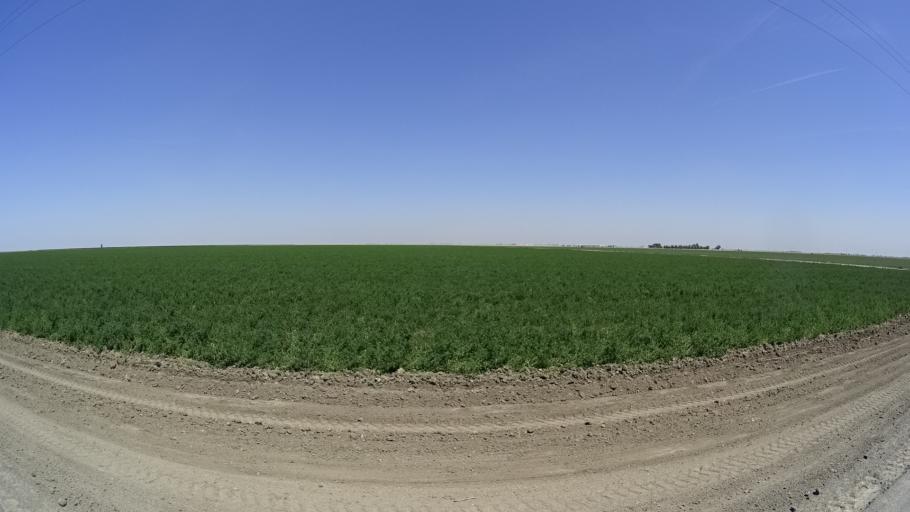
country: US
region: California
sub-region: Kings County
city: Corcoran
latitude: 36.0215
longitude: -119.5822
